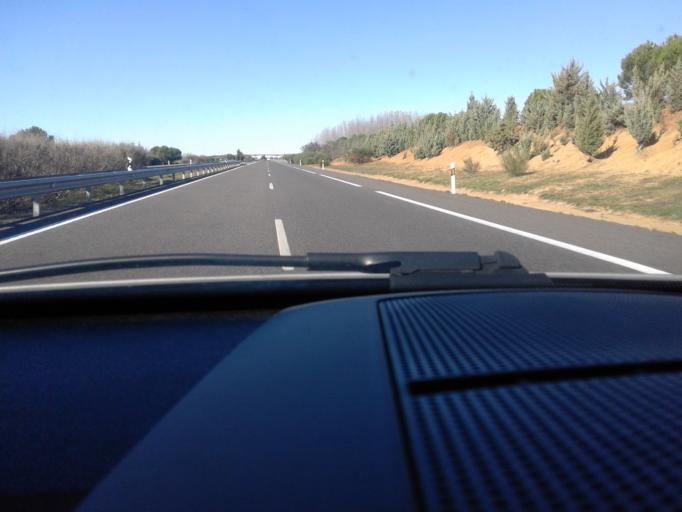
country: ES
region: Castille and Leon
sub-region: Provincia de Leon
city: Bercianos del Real Camino
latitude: 42.3981
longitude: -5.1601
